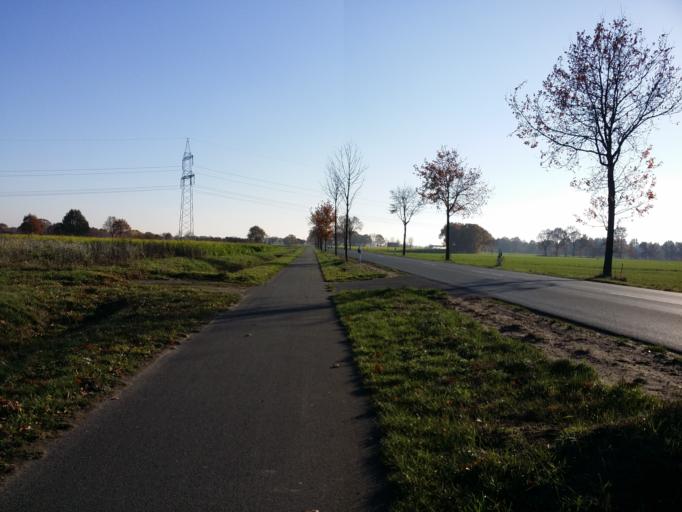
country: DE
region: Lower Saxony
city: Langwedel
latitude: 53.0239
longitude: 9.1647
